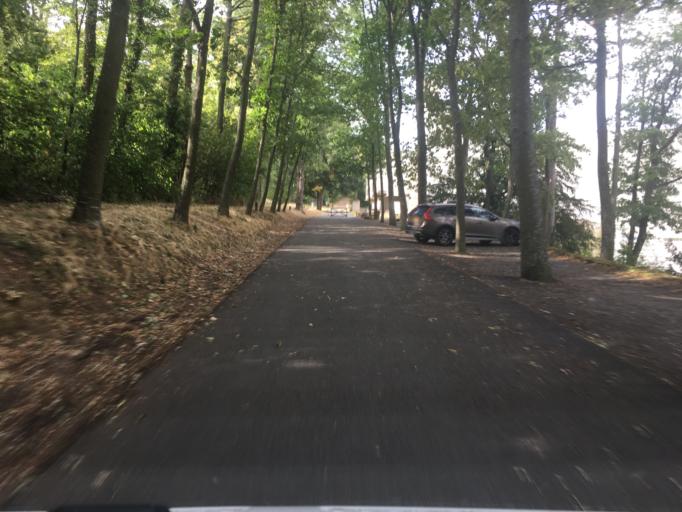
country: FR
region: Rhone-Alpes
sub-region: Departement du Rhone
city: Sourcieux-les-Mines
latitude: 45.8205
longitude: 4.6233
